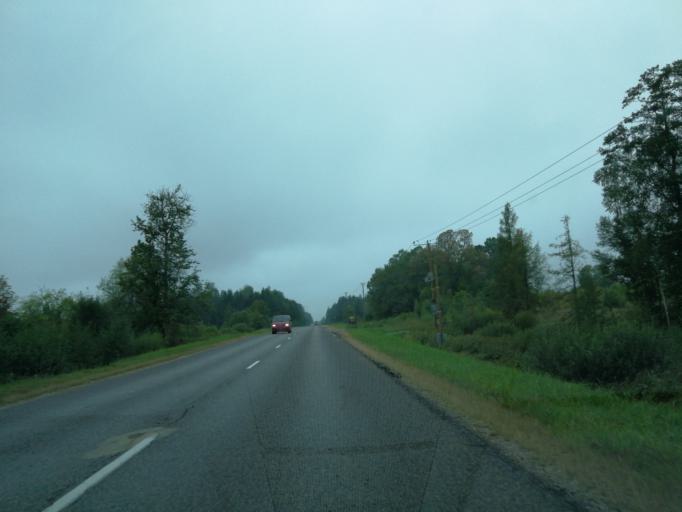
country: LV
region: Varkava
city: Vecvarkava
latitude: 56.3217
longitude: 26.4227
